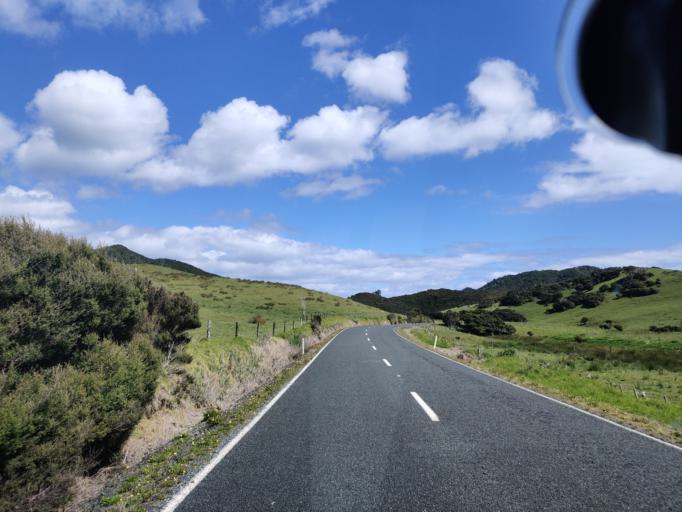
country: NZ
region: Northland
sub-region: Far North District
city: Paihia
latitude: -35.2726
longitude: 174.2804
